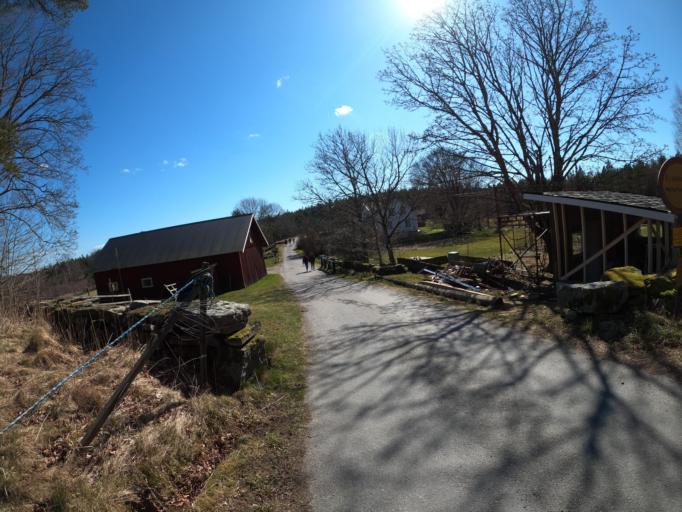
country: SE
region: Vaestra Goetaland
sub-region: Harryda Kommun
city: Molnlycke
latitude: 57.6311
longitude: 12.1203
